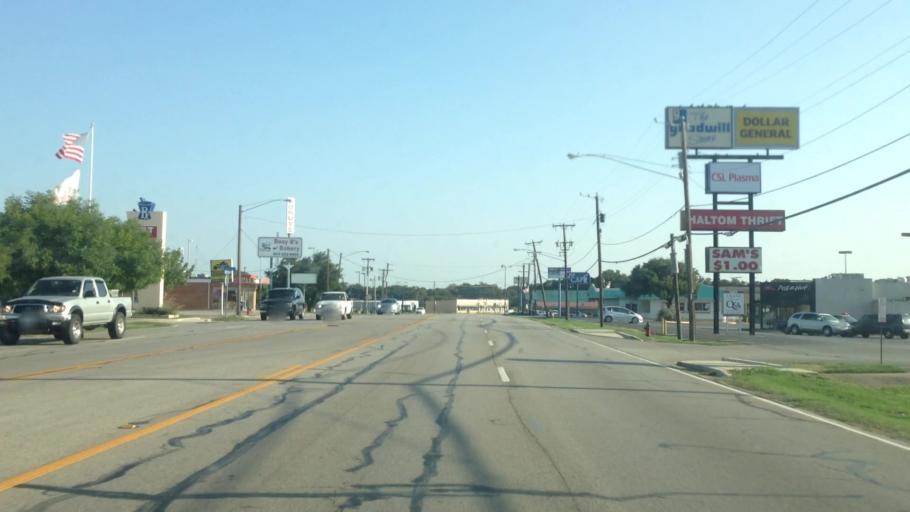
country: US
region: Texas
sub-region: Tarrant County
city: Haltom City
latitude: 32.8043
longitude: -97.2646
